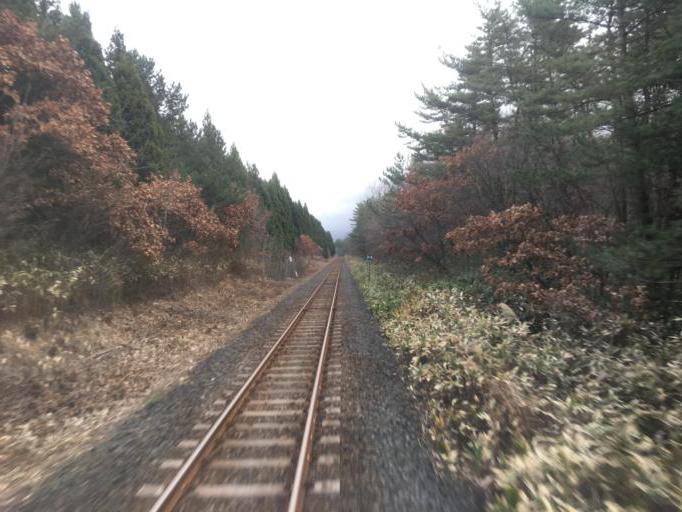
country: JP
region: Aomori
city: Mutsu
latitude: 41.0110
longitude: 141.2386
